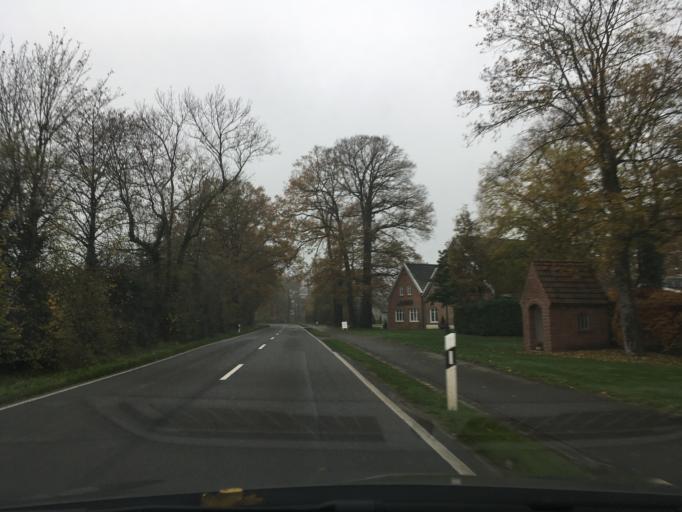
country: DE
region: North Rhine-Westphalia
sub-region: Regierungsbezirk Munster
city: Ahaus
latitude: 52.0811
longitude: 6.9394
